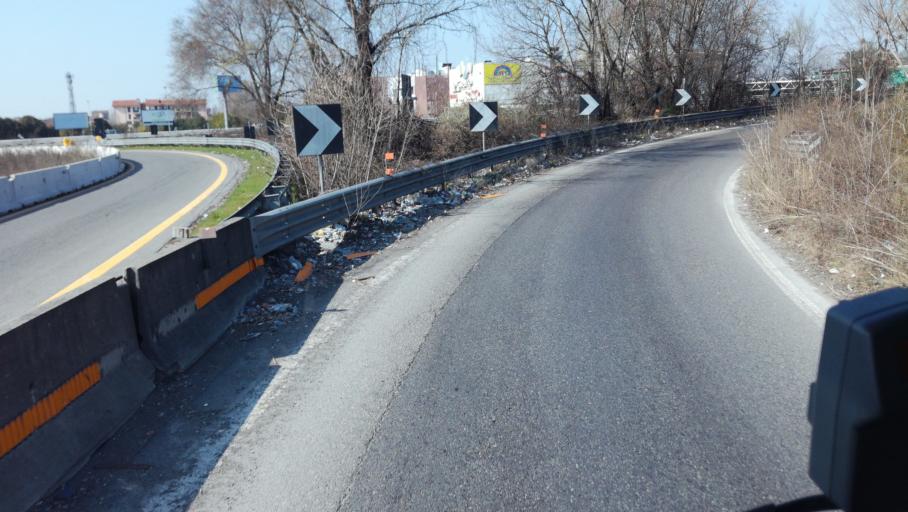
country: IT
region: Lombardy
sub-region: Citta metropolitana di Milano
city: Cormano
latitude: 45.5553
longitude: 9.1663
